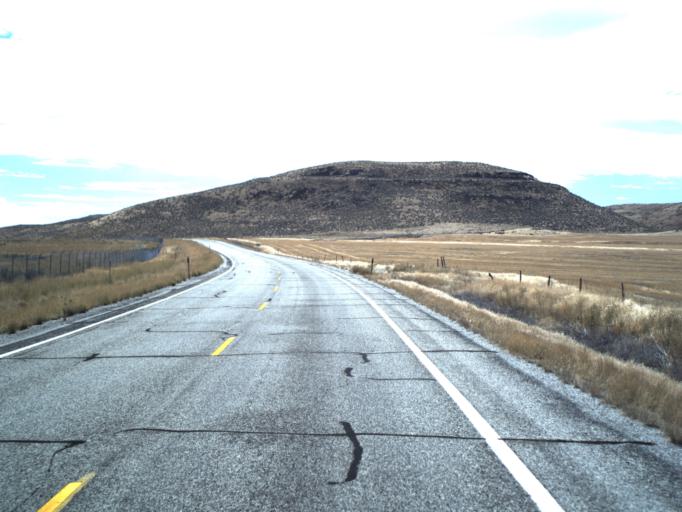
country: US
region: Utah
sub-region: Box Elder County
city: Tremonton
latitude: 41.7151
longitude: -112.4525
